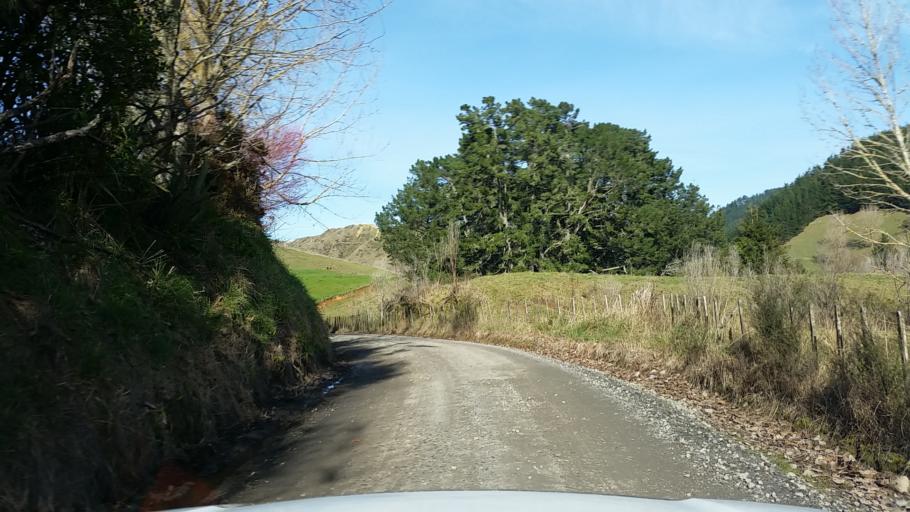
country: NZ
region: Taranaki
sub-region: South Taranaki District
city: Eltham
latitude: -39.3516
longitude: 174.5132
